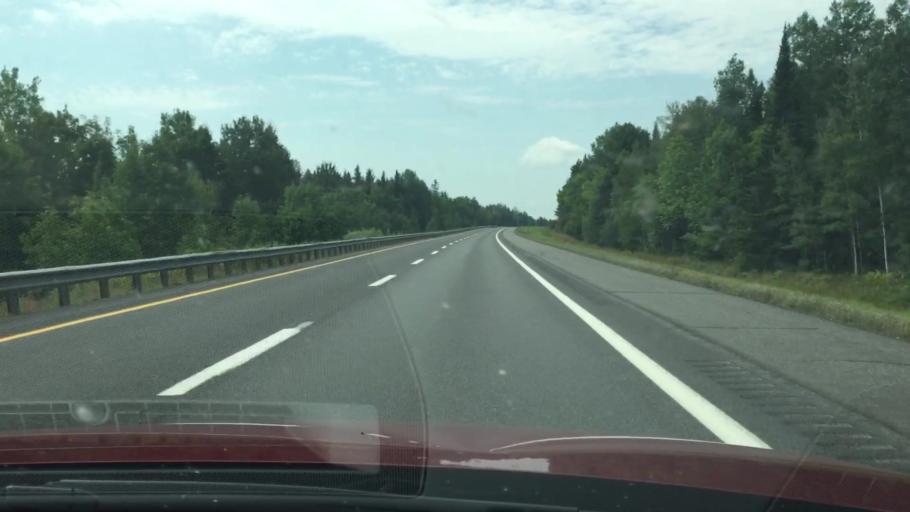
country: US
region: Maine
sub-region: Aroostook County
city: Hodgdon
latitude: 46.1237
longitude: -68.1093
